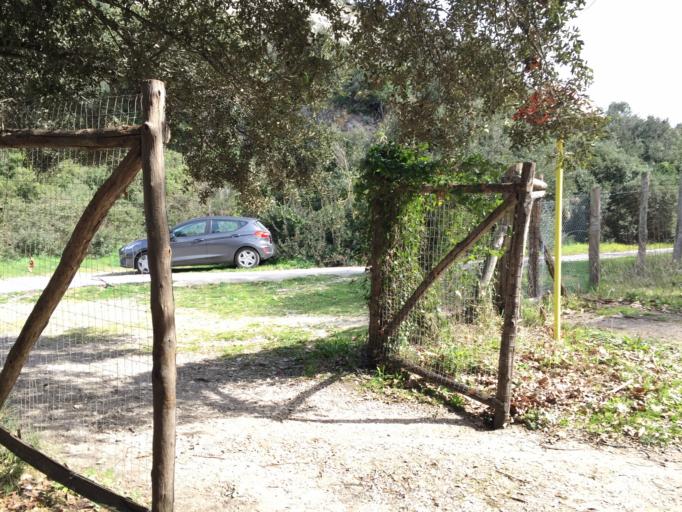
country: IT
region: Campania
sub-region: Provincia di Napoli
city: Monterusciello
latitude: 40.8485
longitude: 14.0496
